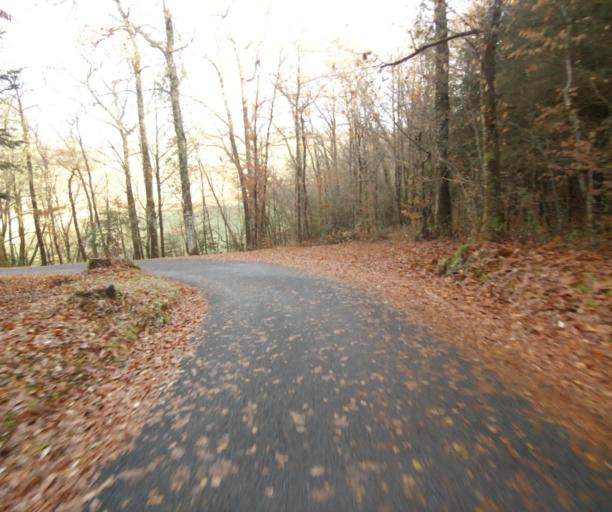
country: FR
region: Limousin
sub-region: Departement de la Correze
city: Chameyrat
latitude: 45.2275
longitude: 1.7358
